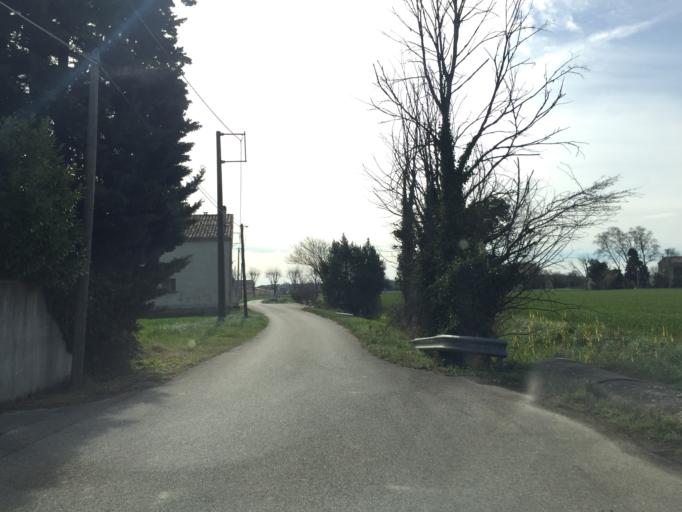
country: FR
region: Provence-Alpes-Cote d'Azur
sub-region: Departement du Vaucluse
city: Caderousse
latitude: 44.1120
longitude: 4.7436
